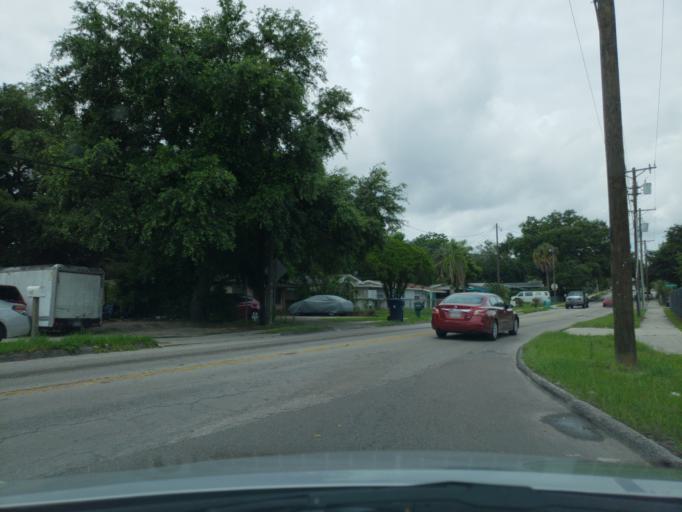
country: US
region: Florida
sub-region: Hillsborough County
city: East Lake-Orient Park
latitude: 28.0034
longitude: -82.4103
